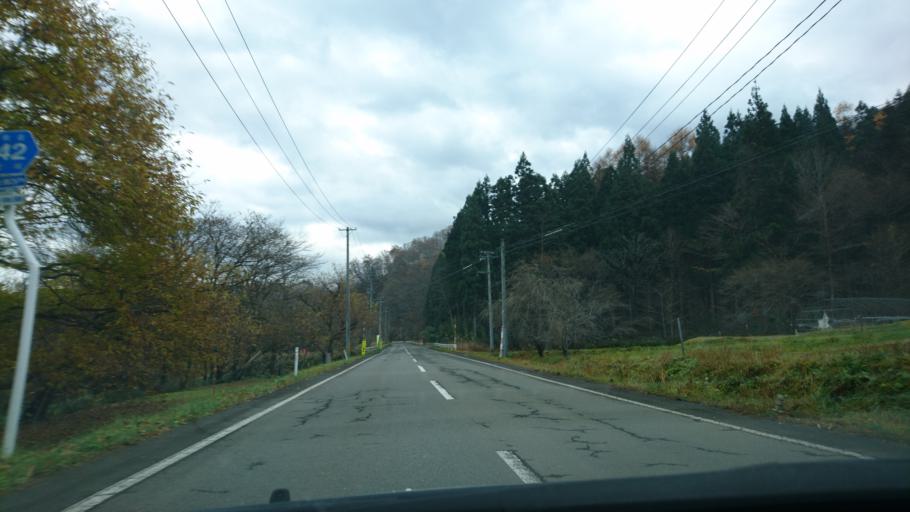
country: JP
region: Iwate
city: Ichinoseki
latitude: 38.9062
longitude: 140.8981
